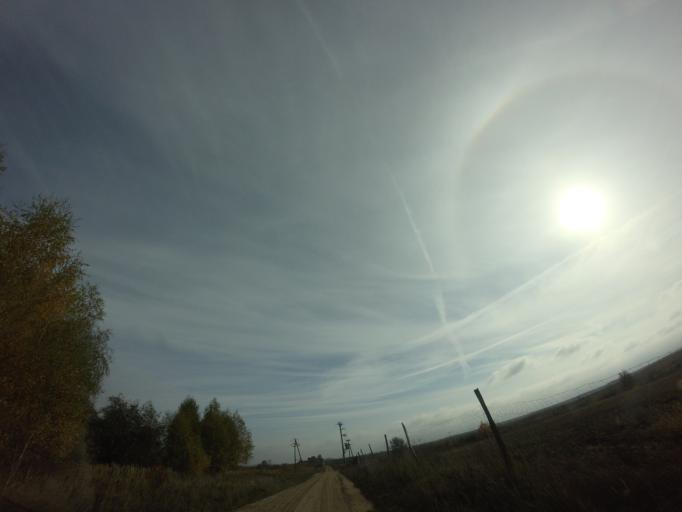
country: PL
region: West Pomeranian Voivodeship
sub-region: Powiat choszczenski
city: Drawno
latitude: 53.2374
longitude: 15.7292
